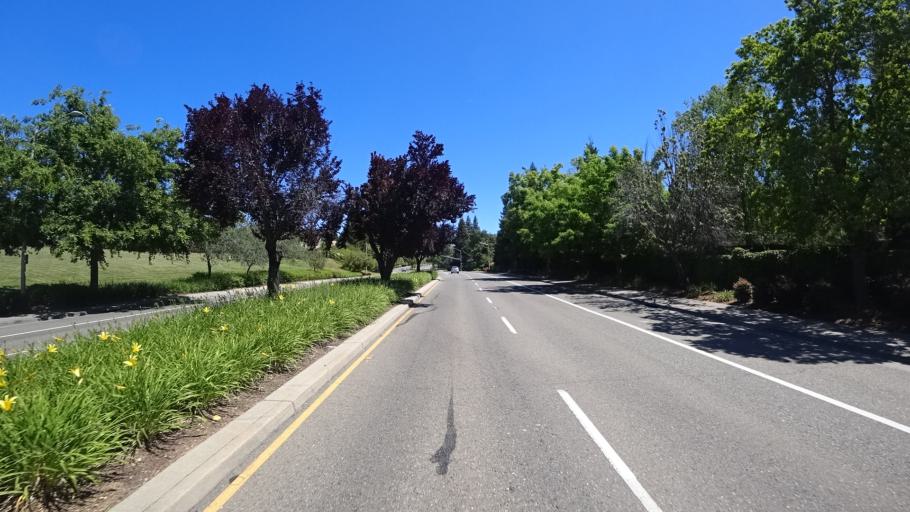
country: US
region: California
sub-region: Placer County
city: Rocklin
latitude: 38.8199
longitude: -121.2514
